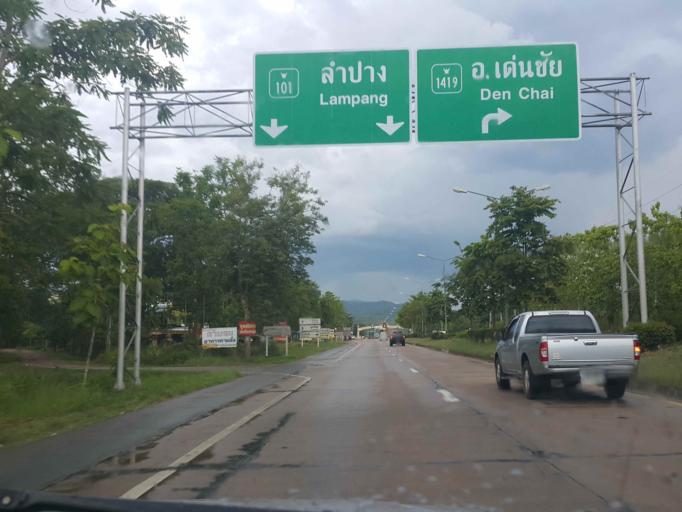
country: TH
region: Phrae
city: Den Chai
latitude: 17.9739
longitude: 100.0794
